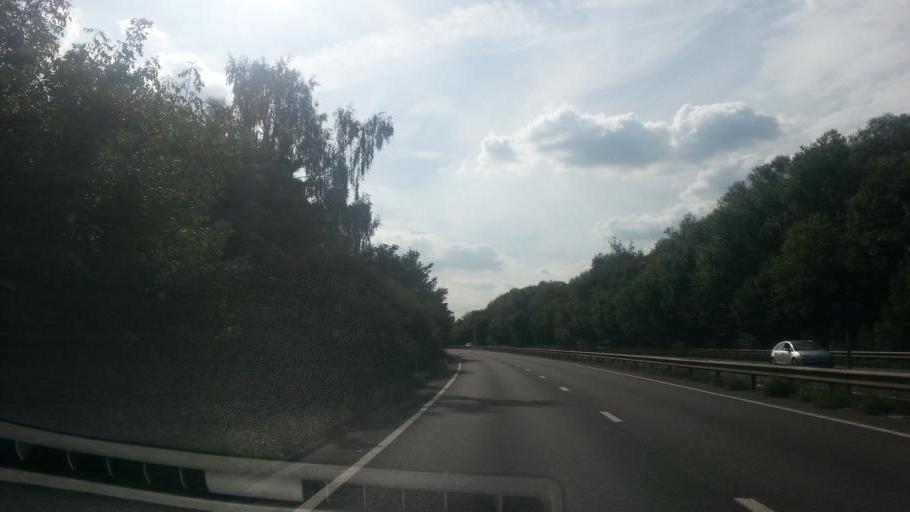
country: GB
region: England
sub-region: Surrey
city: Guildford
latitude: 51.2497
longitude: -0.5788
